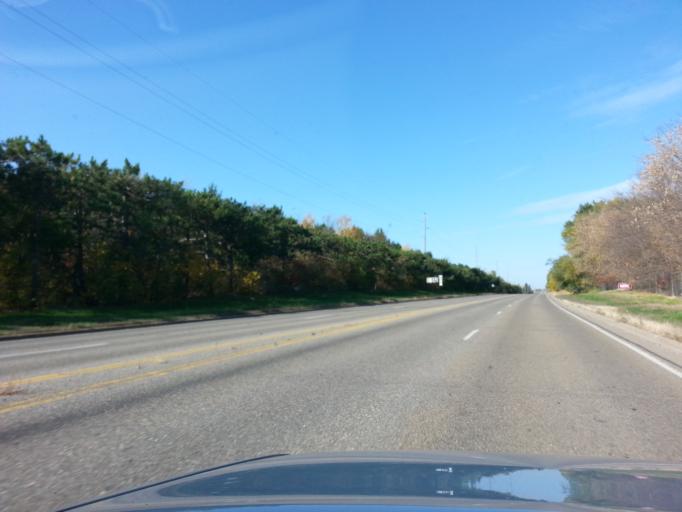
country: US
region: Minnesota
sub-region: Scott County
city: Prior Lake
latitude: 44.6963
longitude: -93.3824
